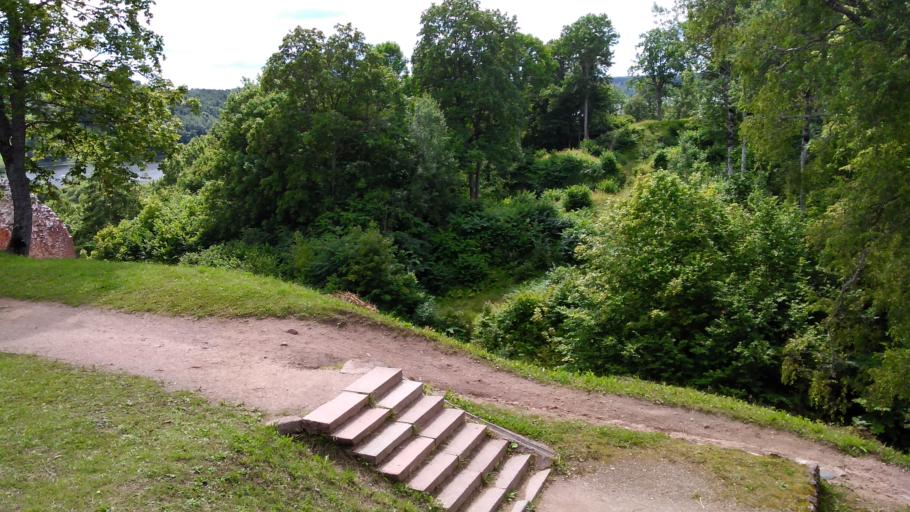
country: EE
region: Viljandimaa
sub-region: Viljandi linn
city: Viljandi
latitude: 58.3590
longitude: 25.5945
